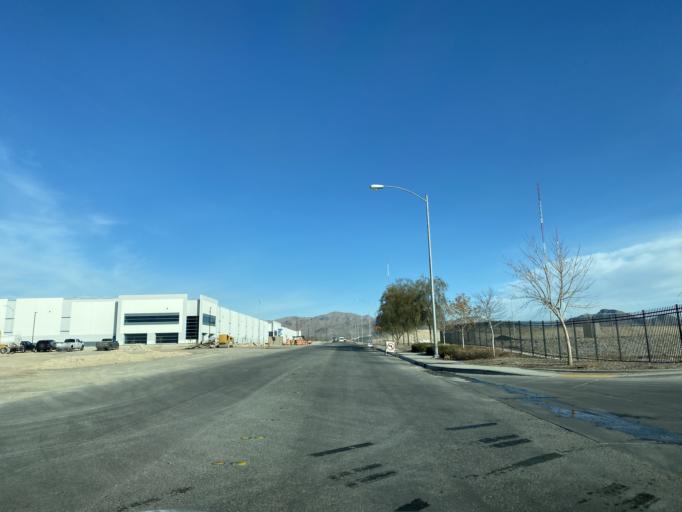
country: US
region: Nevada
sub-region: Clark County
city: Nellis Air Force Base
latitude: 36.2651
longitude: -115.0478
